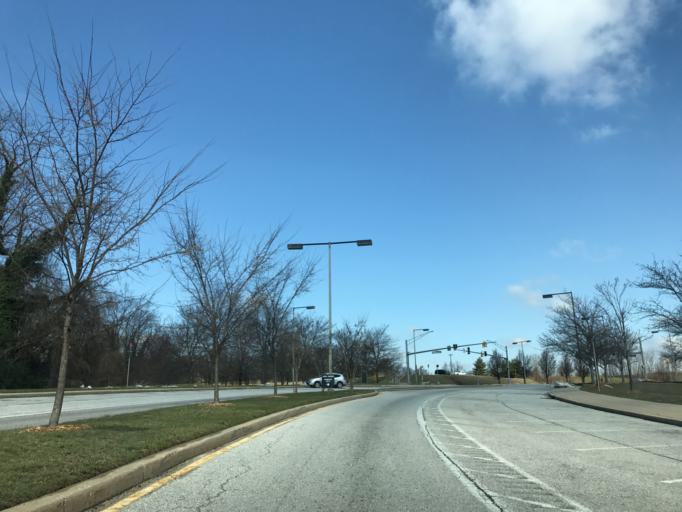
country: US
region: Maryland
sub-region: Baltimore County
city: Arbutus
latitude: 39.2551
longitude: -76.7164
